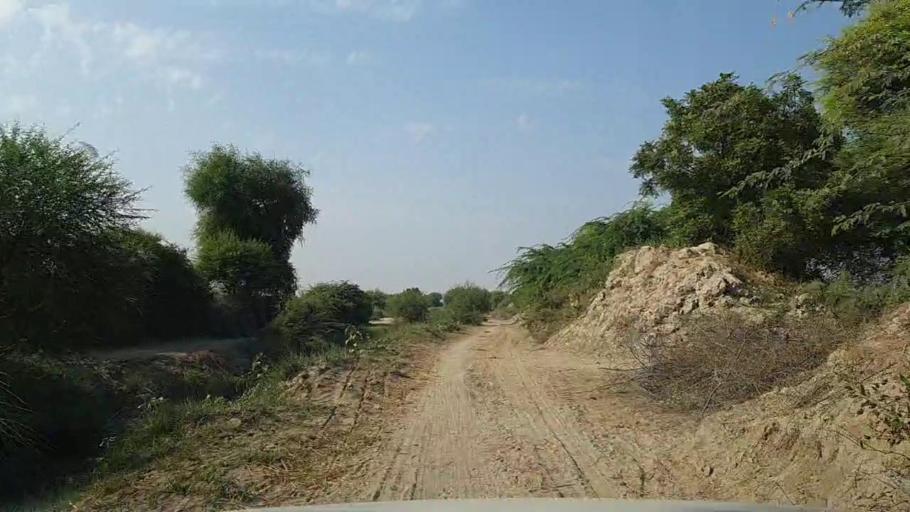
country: PK
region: Sindh
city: Mirpur Batoro
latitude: 24.7094
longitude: 68.2986
